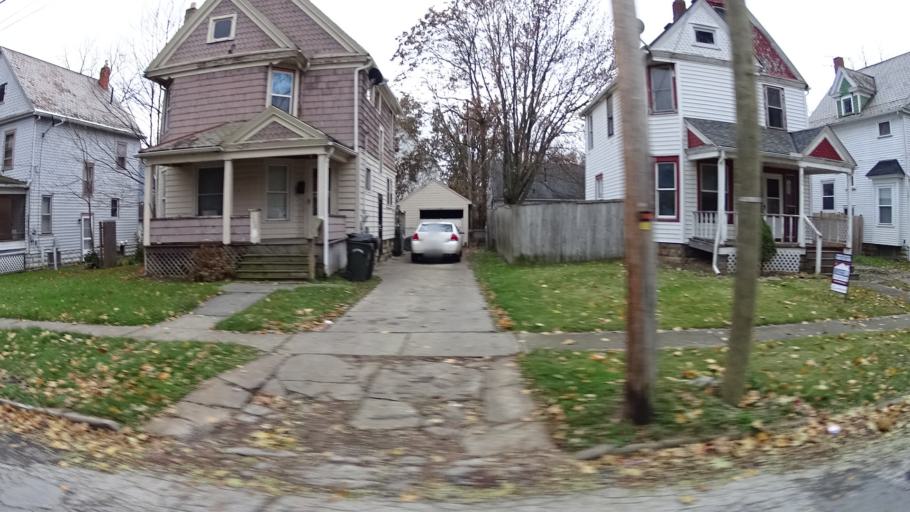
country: US
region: Ohio
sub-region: Lorain County
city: Elyria
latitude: 41.3560
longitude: -82.1060
